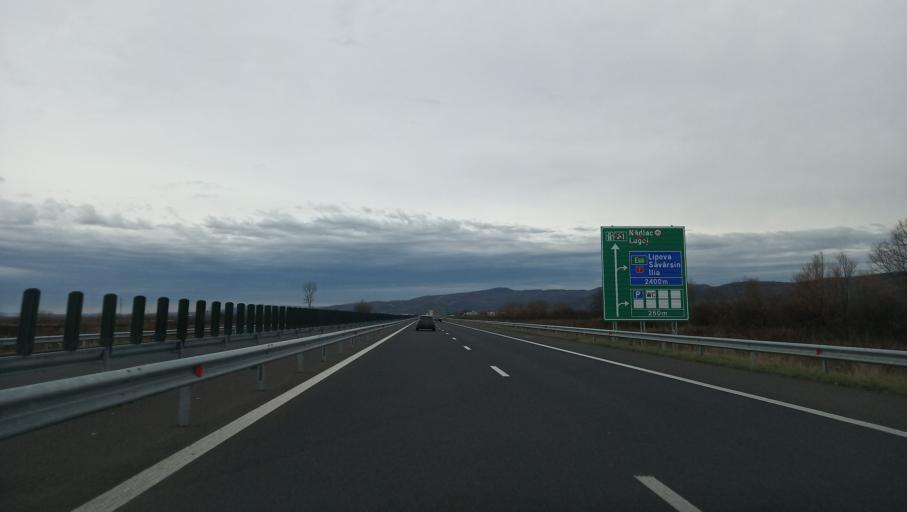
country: RO
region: Hunedoara
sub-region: Comuna Ilia
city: Ilia
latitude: 45.9470
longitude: 22.6638
